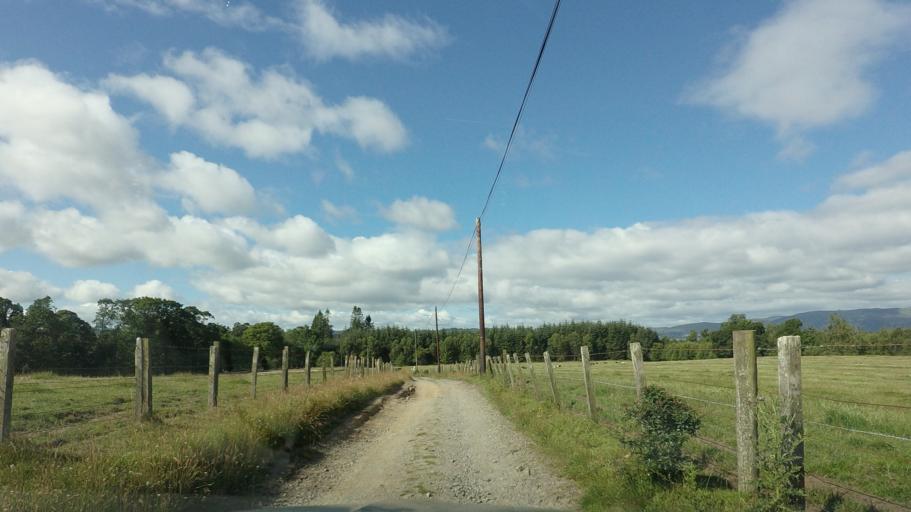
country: GB
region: Scotland
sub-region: Stirling
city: Killearn
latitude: 56.0710
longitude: -4.4761
